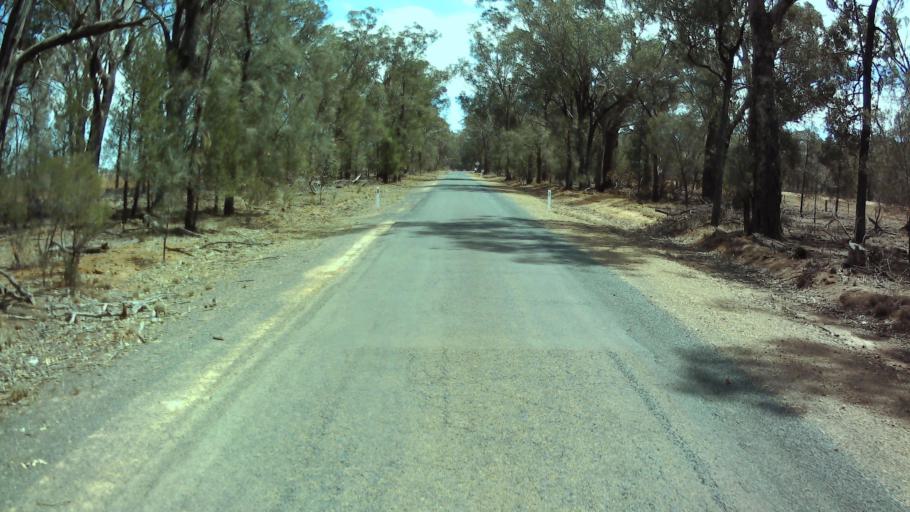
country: AU
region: New South Wales
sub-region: Weddin
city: Grenfell
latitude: -33.6464
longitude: 148.1919
